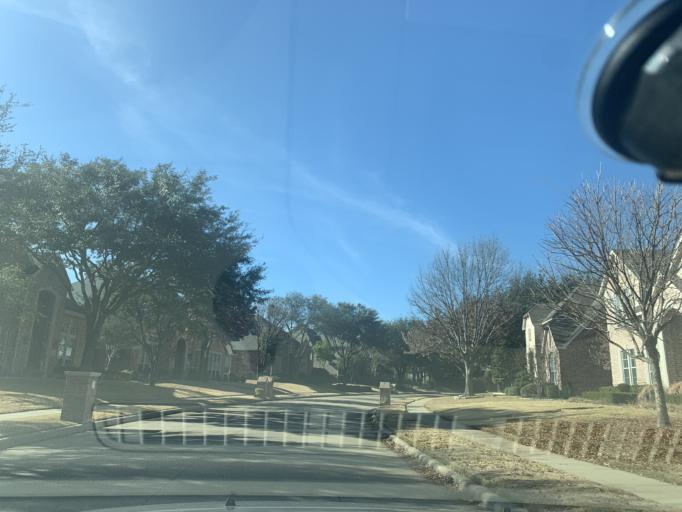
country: US
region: Texas
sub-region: Denton County
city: The Colony
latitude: 33.0540
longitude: -96.8149
